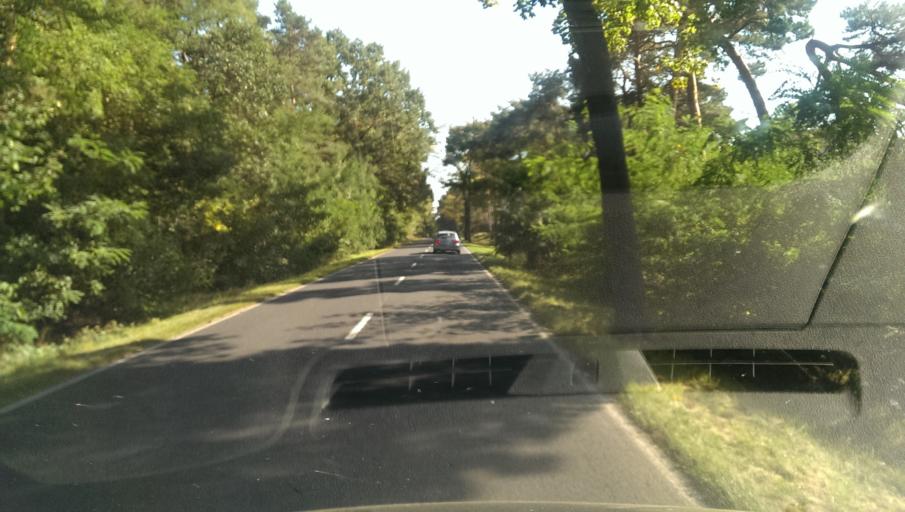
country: DE
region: Brandenburg
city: Teupitz
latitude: 52.1277
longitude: 13.6287
